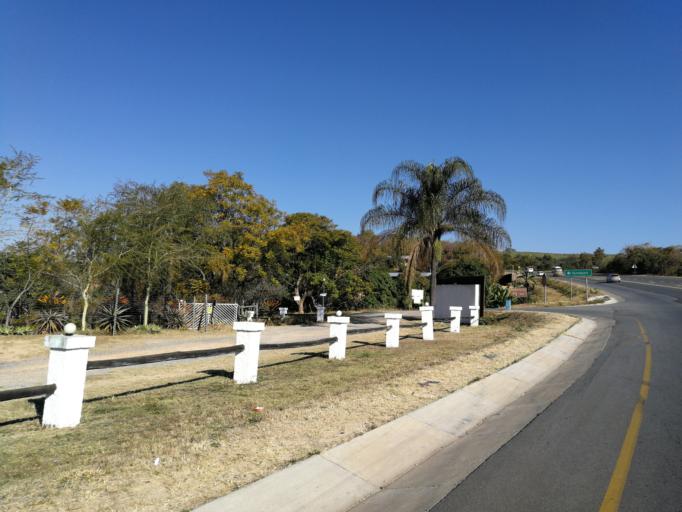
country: ZA
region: Mpumalanga
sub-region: Ehlanzeni District
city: White River
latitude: -25.0657
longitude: 31.1076
